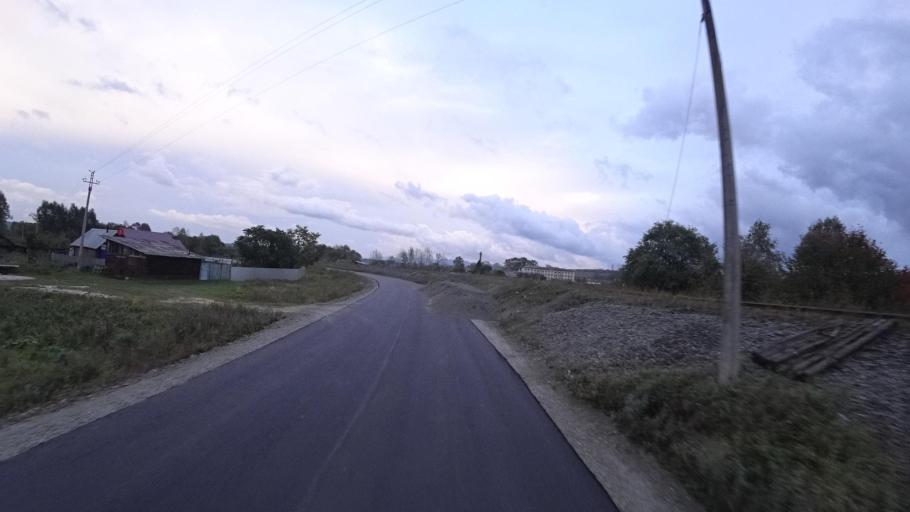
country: RU
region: Jewish Autonomous Oblast
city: Izvestkovyy
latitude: 48.9896
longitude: 131.5477
